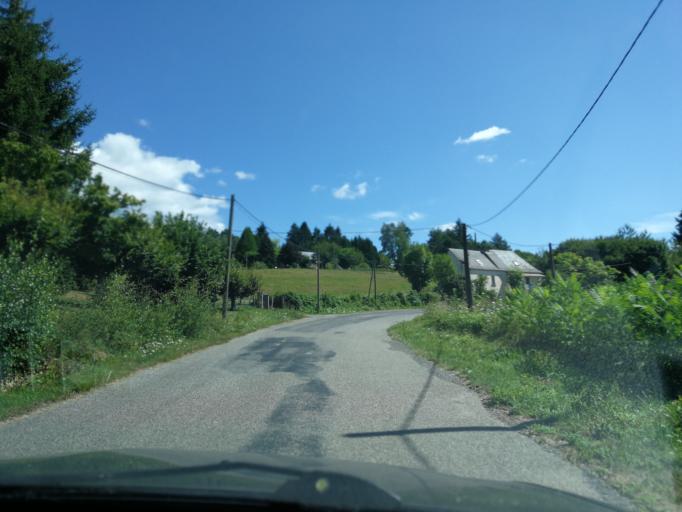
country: FR
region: Limousin
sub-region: Departement de la Correze
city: Argentat
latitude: 45.1037
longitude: 1.8816
